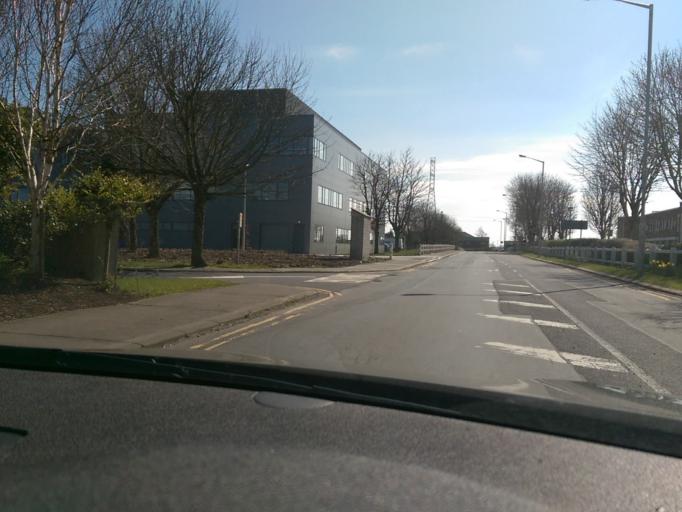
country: IE
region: Connaught
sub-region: County Galway
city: Gaillimh
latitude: 53.2931
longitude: -9.0080
